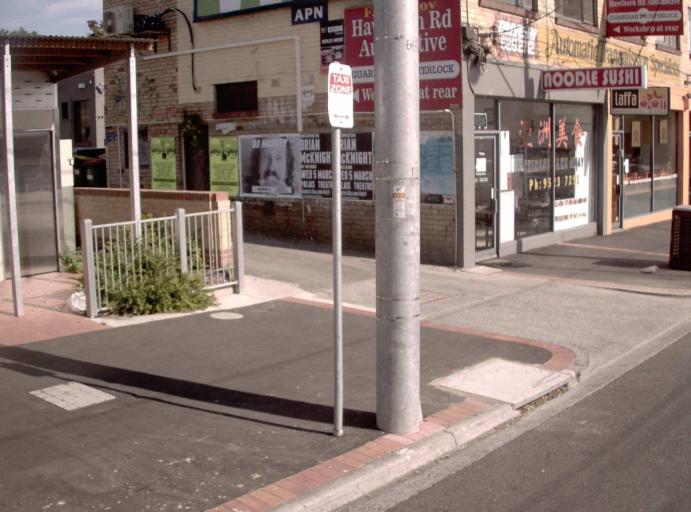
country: AU
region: Victoria
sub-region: Glen Eira
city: Caulfield
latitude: -37.8866
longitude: 145.0220
